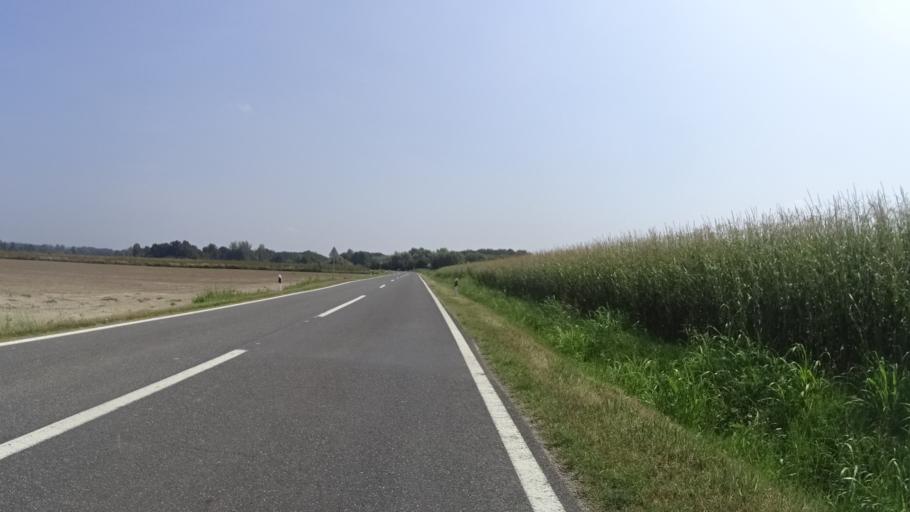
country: HR
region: Medimurska
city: Hodosan
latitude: 46.3995
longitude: 16.6525
